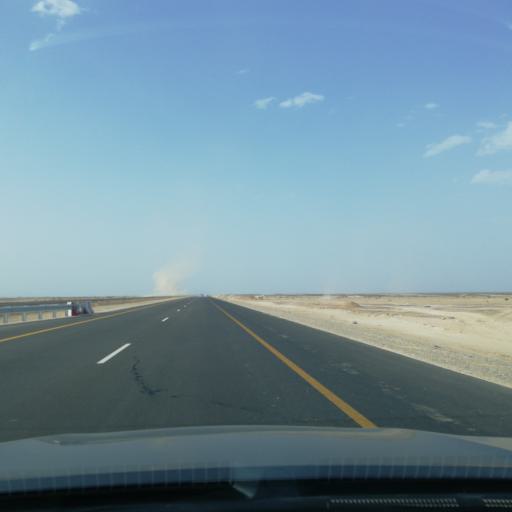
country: OM
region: Muhafazat ad Dakhiliyah
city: Adam
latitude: 22.0992
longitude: 57.5198
